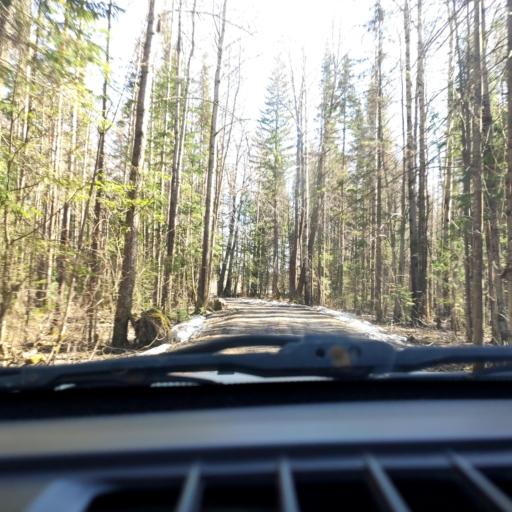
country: RU
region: Perm
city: Kultayevo
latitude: 57.8223
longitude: 55.7951
